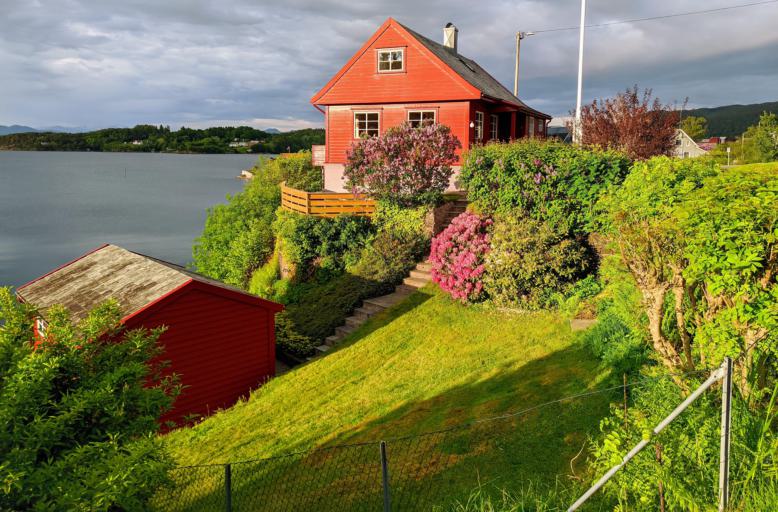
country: NO
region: Hordaland
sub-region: Tysnes
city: Uggdal
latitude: 60.0438
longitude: 5.5244
